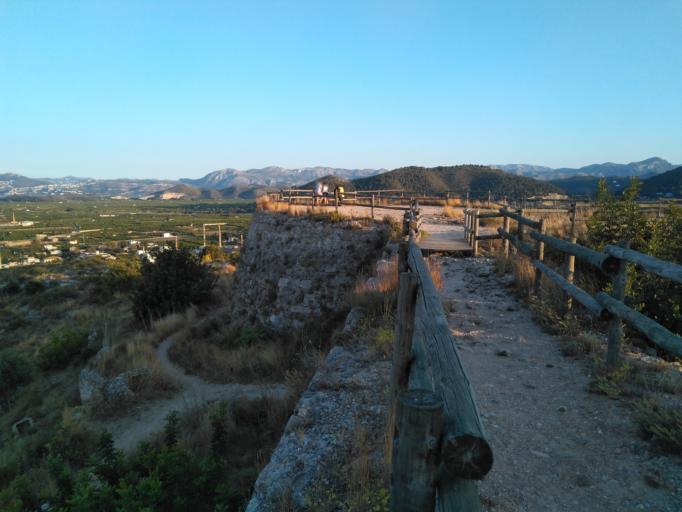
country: ES
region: Valencia
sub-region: Provincia de Valencia
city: Oliva
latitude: 38.9169
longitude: -0.1211
